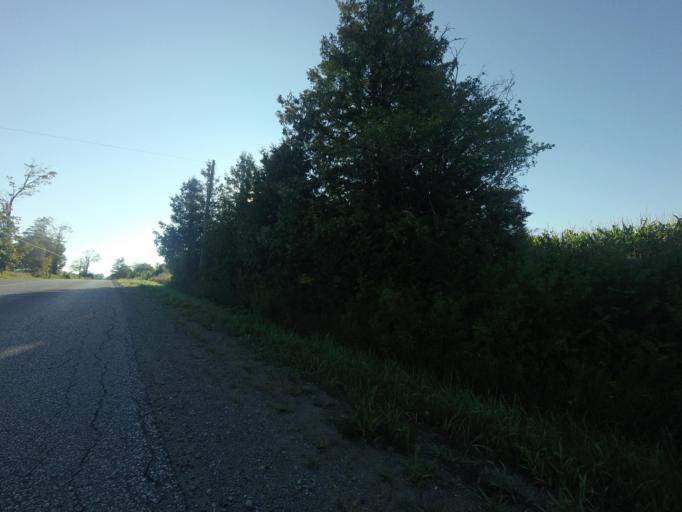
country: CA
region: Ontario
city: Bradford West Gwillimbury
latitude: 44.0369
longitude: -79.7978
